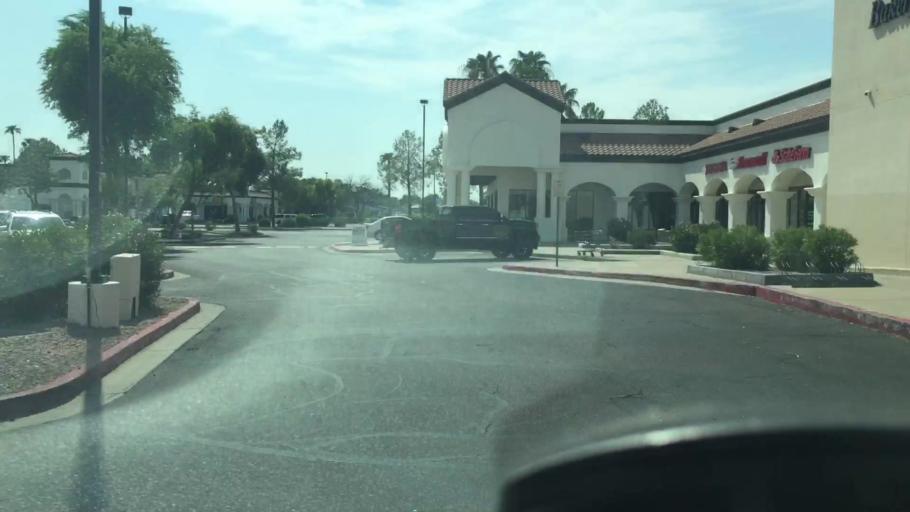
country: US
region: Arizona
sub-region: Maricopa County
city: Gilbert
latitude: 33.3782
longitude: -111.7516
